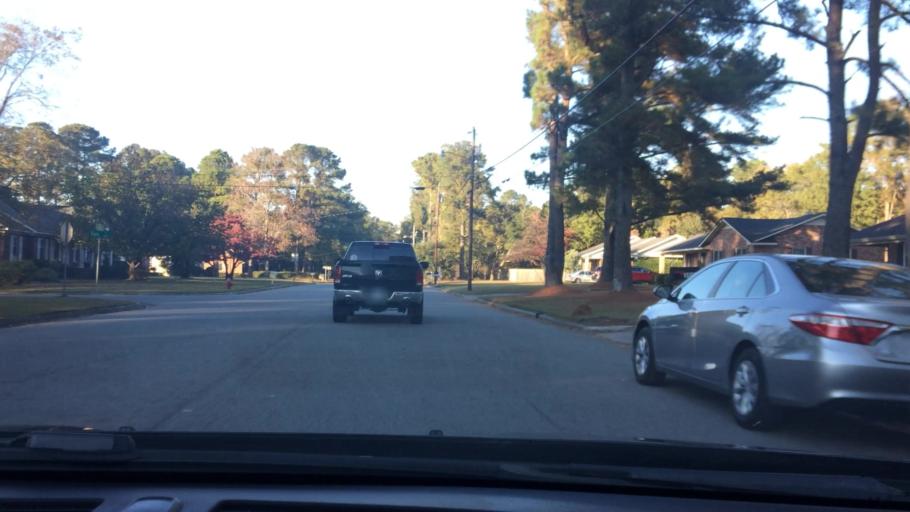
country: US
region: North Carolina
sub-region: Pitt County
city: Greenville
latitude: 35.5855
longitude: -77.3613
